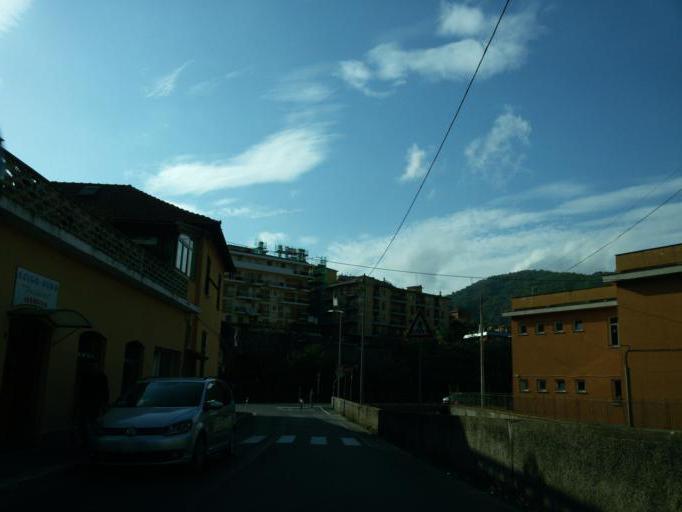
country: IT
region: Liguria
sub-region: Provincia di Genova
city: Piccarello
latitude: 44.4607
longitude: 8.9790
